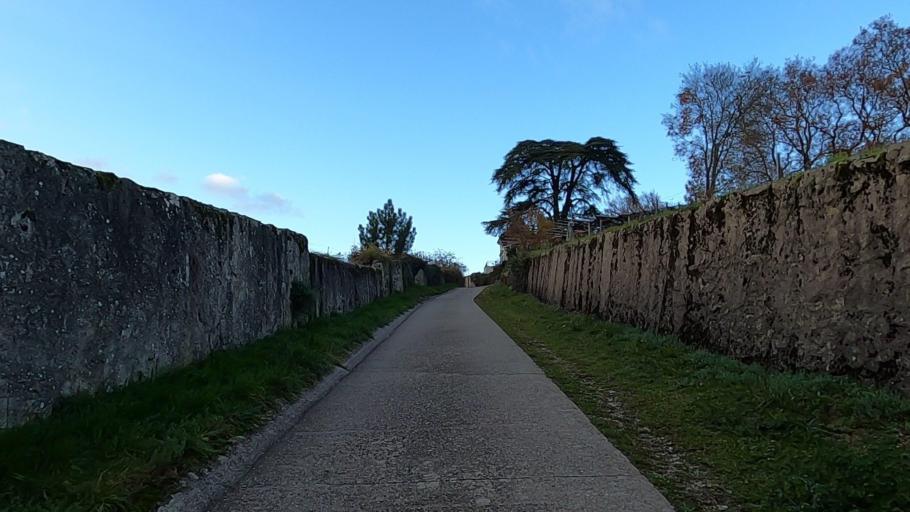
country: CH
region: Vaud
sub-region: Morges District
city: Saint-Prex
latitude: 46.5165
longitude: 6.4600
